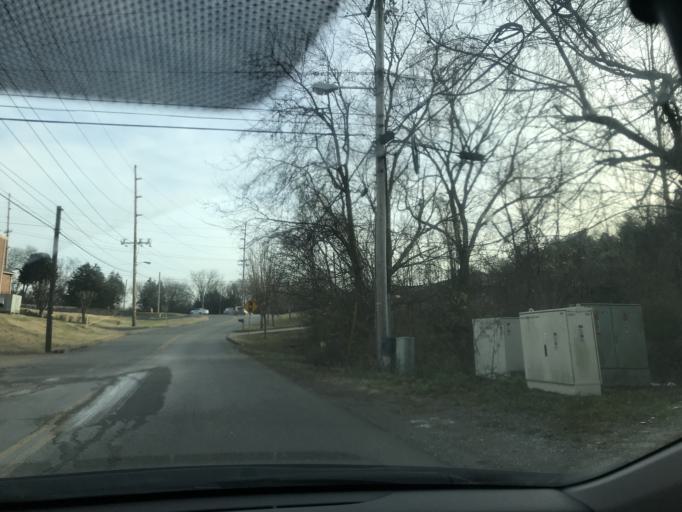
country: US
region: Tennessee
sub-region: Davidson County
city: Nashville
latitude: 36.2038
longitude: -86.8211
